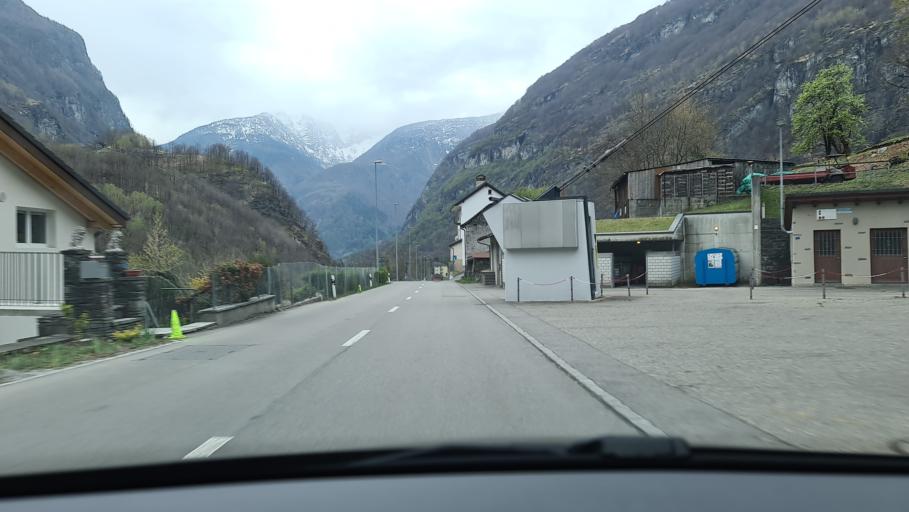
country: CH
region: Ticino
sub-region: Vallemaggia District
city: Cevio
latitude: 46.3466
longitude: 8.6121
